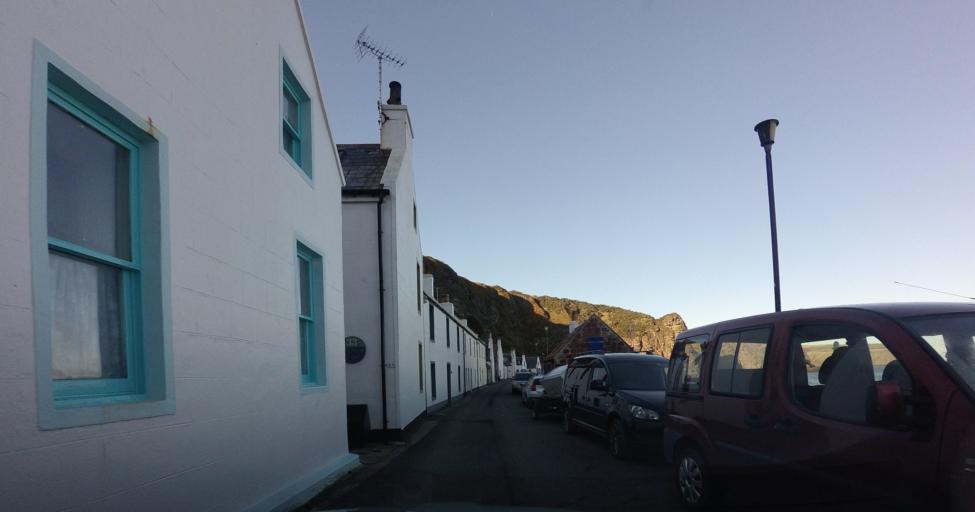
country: GB
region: Scotland
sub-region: Aberdeenshire
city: Rosehearty
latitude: 57.6789
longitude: -2.2603
